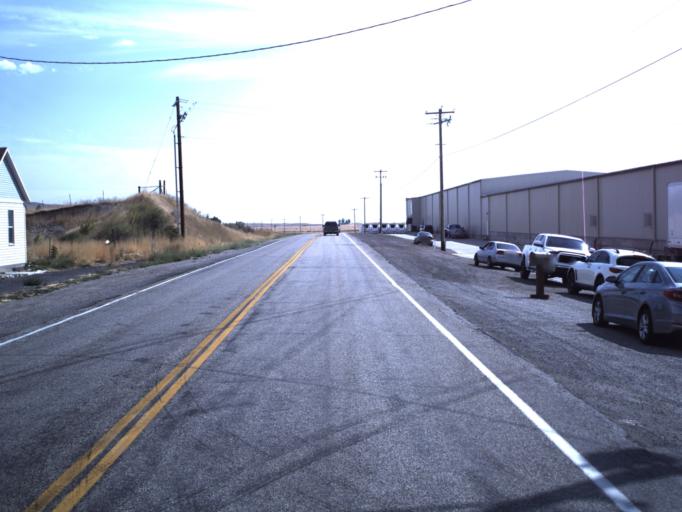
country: US
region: Utah
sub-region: Box Elder County
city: Garland
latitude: 41.7740
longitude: -112.0956
